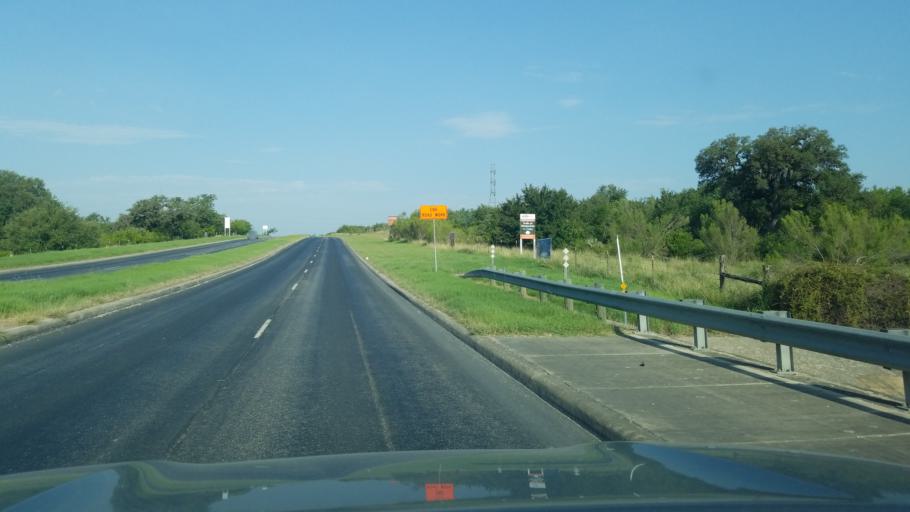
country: US
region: Texas
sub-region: Bexar County
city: Leon Valley
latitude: 29.4656
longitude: -98.7144
